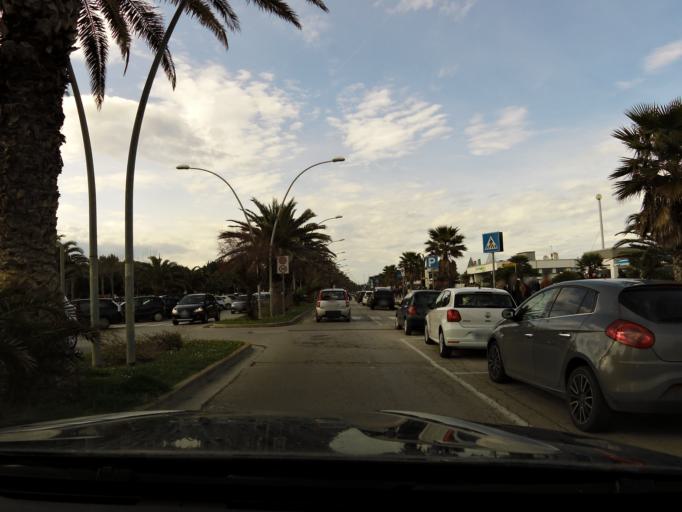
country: IT
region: The Marches
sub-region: Provincia di Macerata
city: Portocivitanova
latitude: 43.3049
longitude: 13.7353
